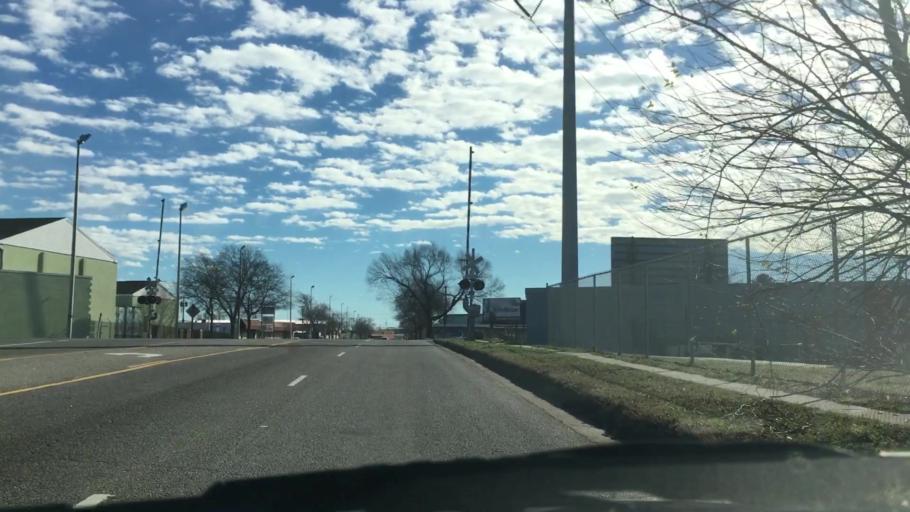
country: US
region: Virginia
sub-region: City of Norfolk
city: Norfolk
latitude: 36.8675
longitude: -76.2493
